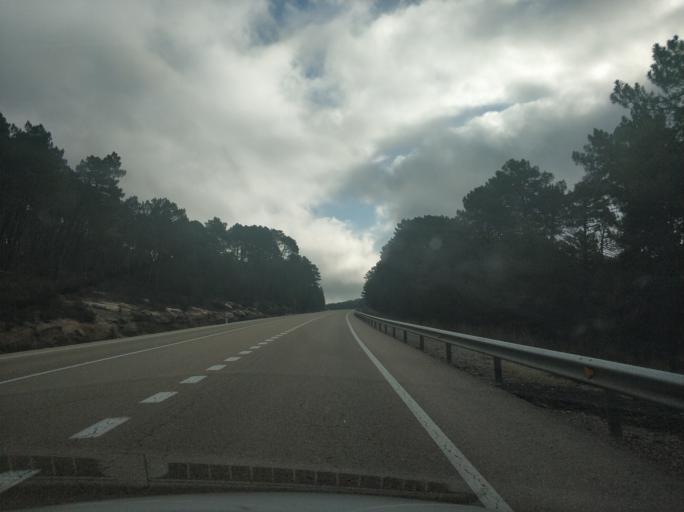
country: ES
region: Castille and Leon
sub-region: Provincia de Soria
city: Navaleno
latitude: 41.8312
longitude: -2.9815
